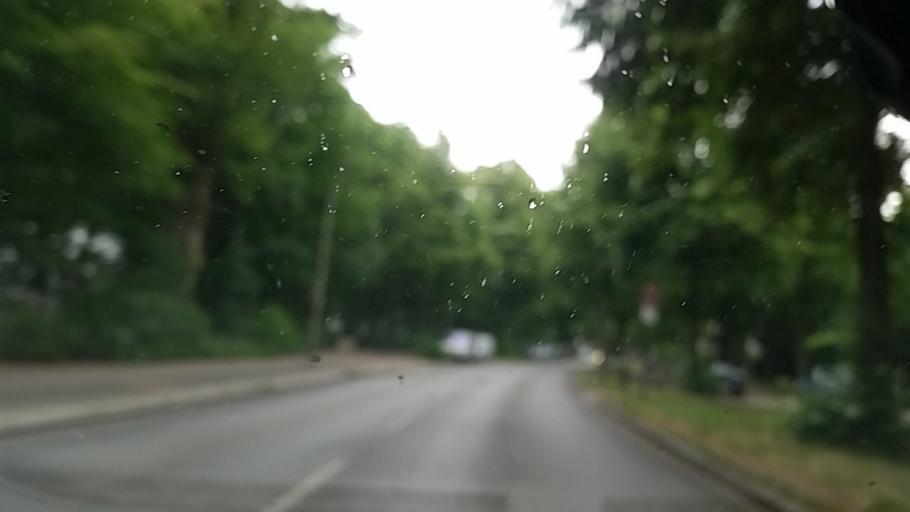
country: DE
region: Hamburg
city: Altona
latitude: 53.5611
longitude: 9.9073
